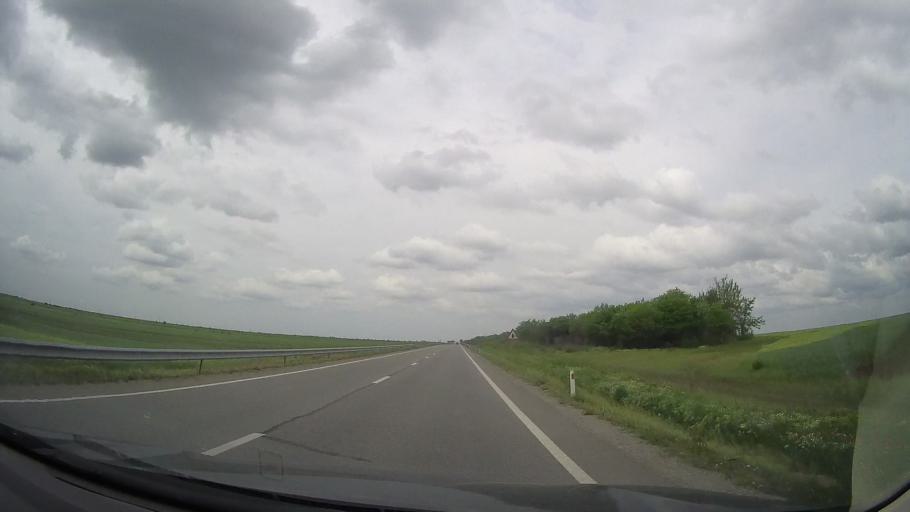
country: RO
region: Dolj
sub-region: Comuna Diosti
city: Radomir
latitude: 44.1316
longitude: 24.1465
